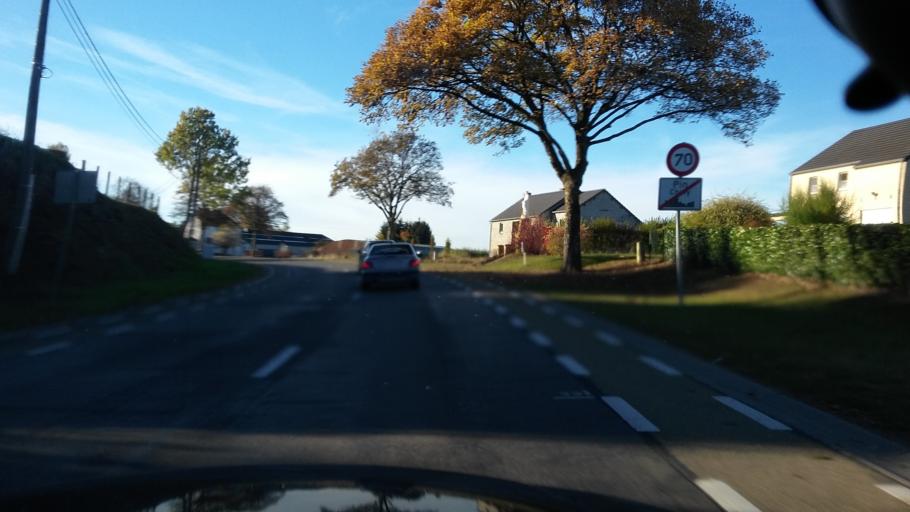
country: BE
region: Wallonia
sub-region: Province du Luxembourg
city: Chiny
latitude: 49.6881
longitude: 5.3641
